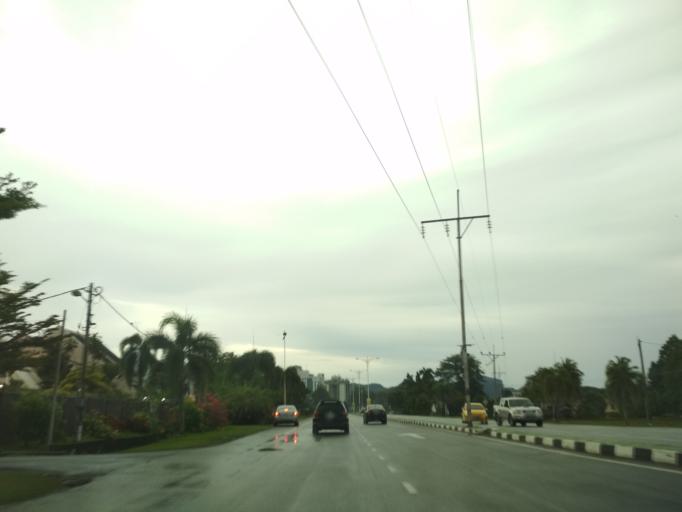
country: MY
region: Perlis
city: Kangar
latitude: 6.4396
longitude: 100.2088
